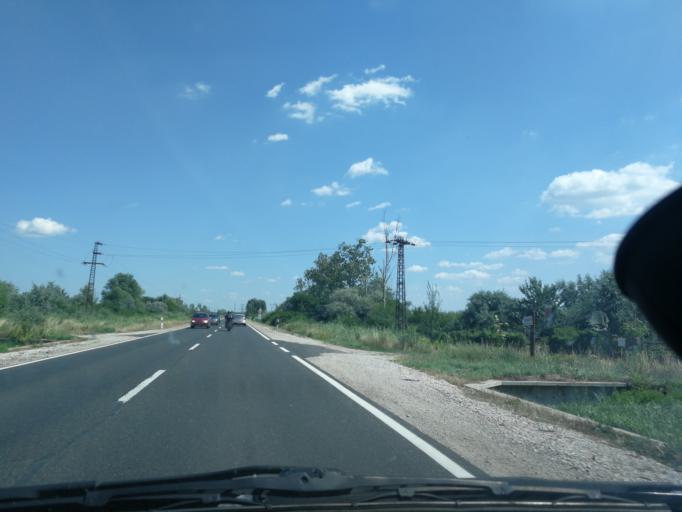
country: HU
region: Fejer
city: Pakozd
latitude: 47.1825
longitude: 18.5324
